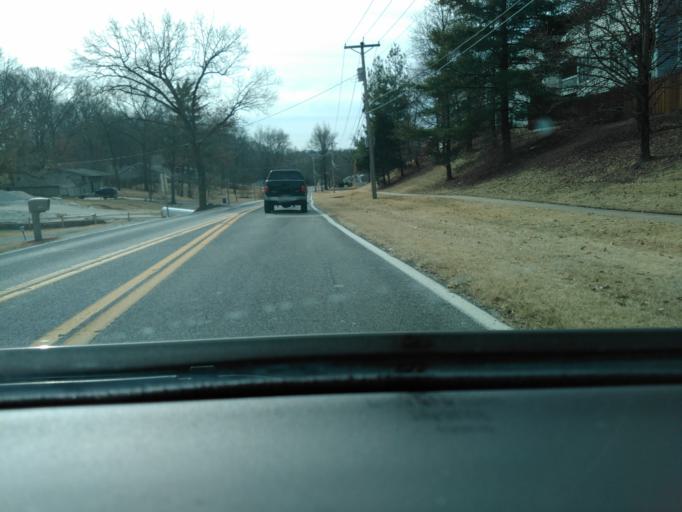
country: US
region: Missouri
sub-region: Saint Louis County
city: Valley Park
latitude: 38.5591
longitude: -90.5111
